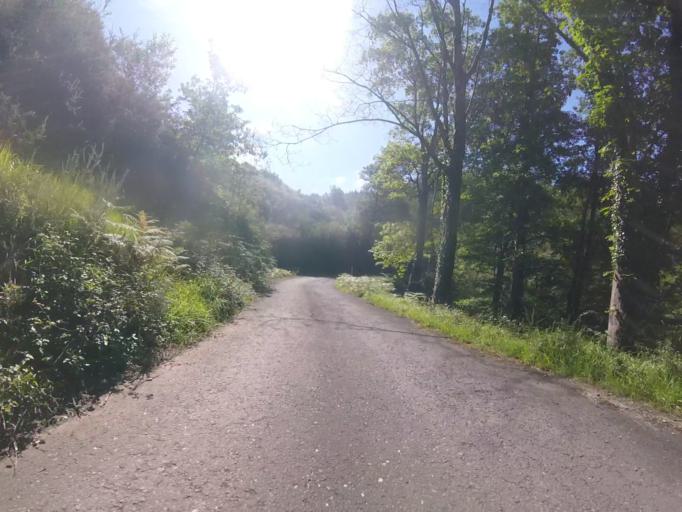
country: ES
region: Navarre
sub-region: Provincia de Navarra
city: Goizueta
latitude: 43.1872
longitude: -1.8312
